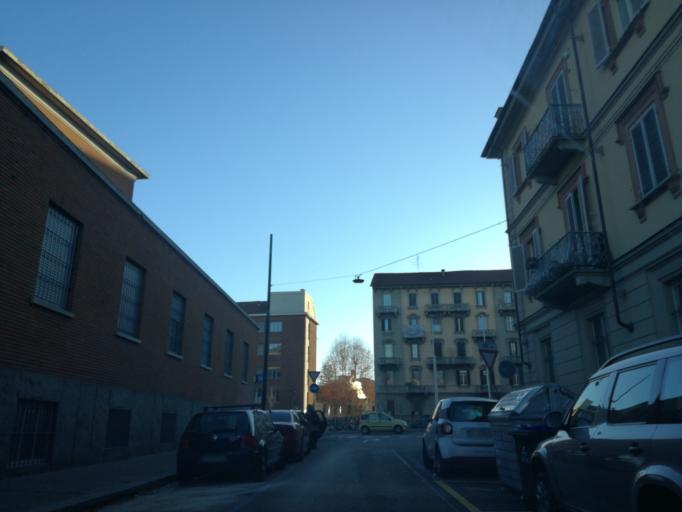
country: IT
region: Piedmont
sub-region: Provincia di Torino
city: Turin
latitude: 45.0799
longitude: 7.6699
